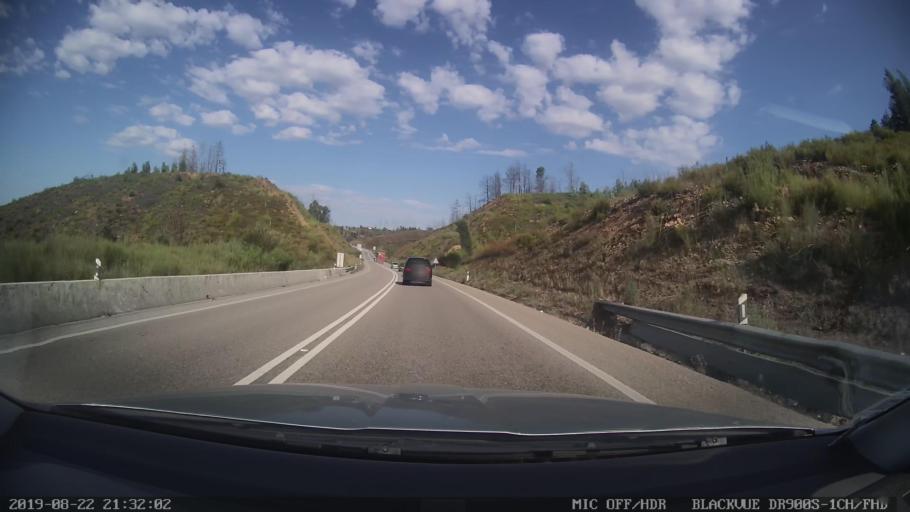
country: PT
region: Leiria
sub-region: Pedrogao Grande
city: Pedrogao Grande
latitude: 39.9254
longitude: -8.1592
